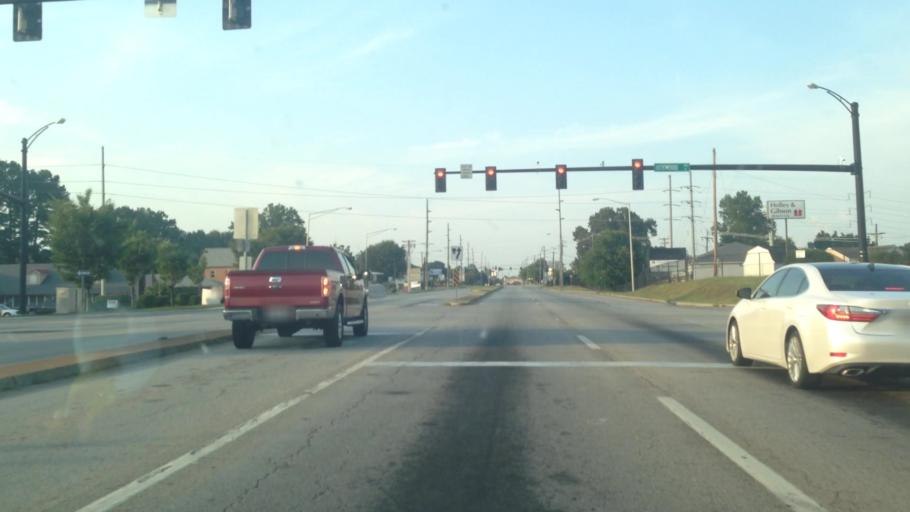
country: US
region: Virginia
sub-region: City of Danville
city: Danville
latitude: 36.6016
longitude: -79.4146
